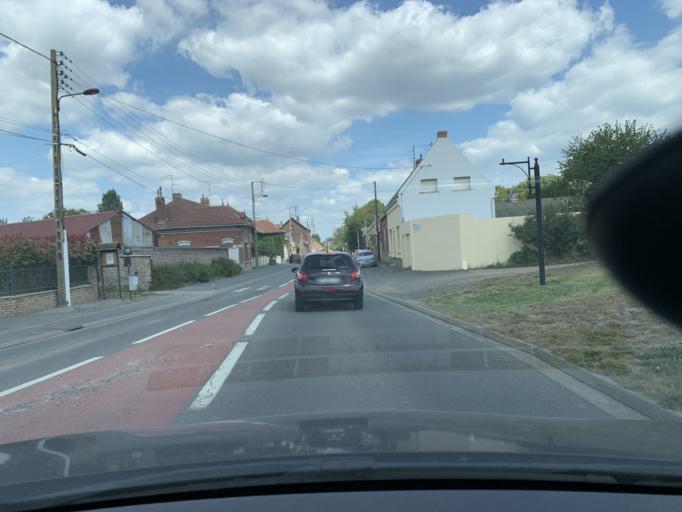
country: FR
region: Nord-Pas-de-Calais
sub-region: Departement du Nord
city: Goeulzin
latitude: 50.3132
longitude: 3.0973
